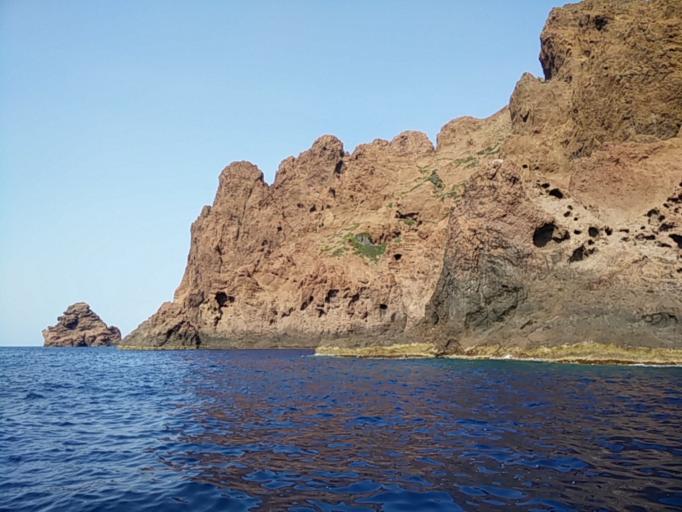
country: FR
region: Corsica
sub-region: Departement de la Corse-du-Sud
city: Cargese
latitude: 42.3737
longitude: 8.5438
